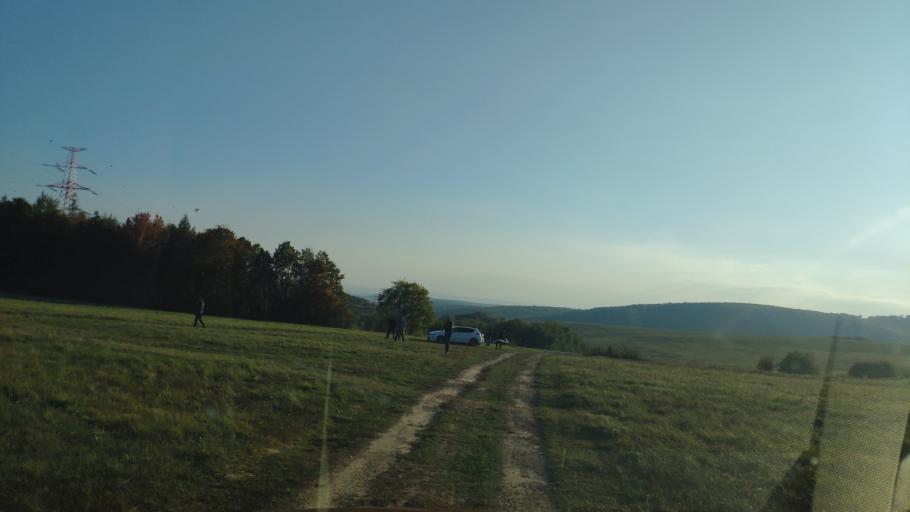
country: SK
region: Kosicky
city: Kosice
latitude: 48.7096
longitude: 21.1681
